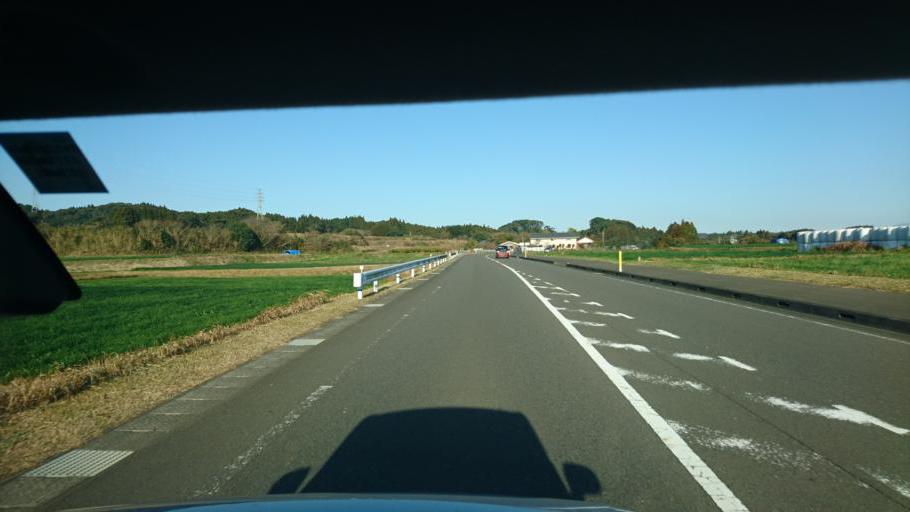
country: JP
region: Miyazaki
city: Miyazaki-shi
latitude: 31.8516
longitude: 131.3767
